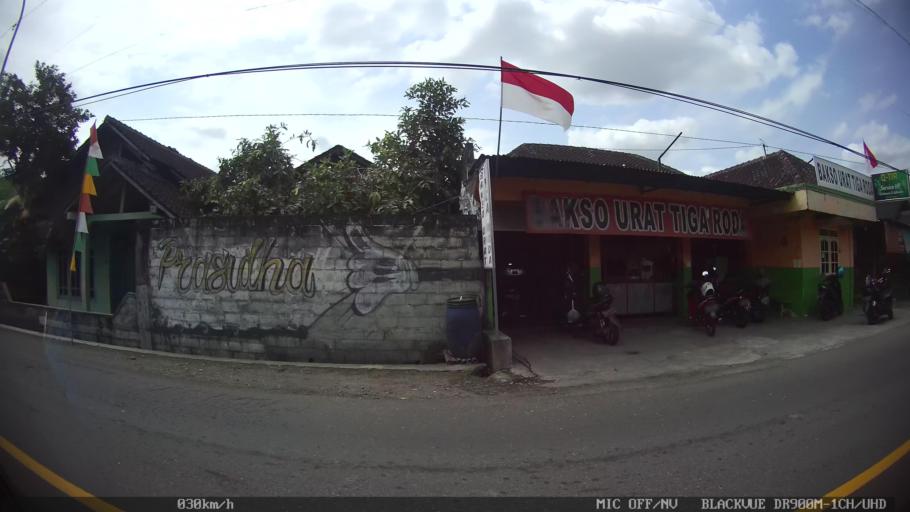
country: ID
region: Central Java
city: Candi Prambanan
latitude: -7.7346
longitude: 110.4784
